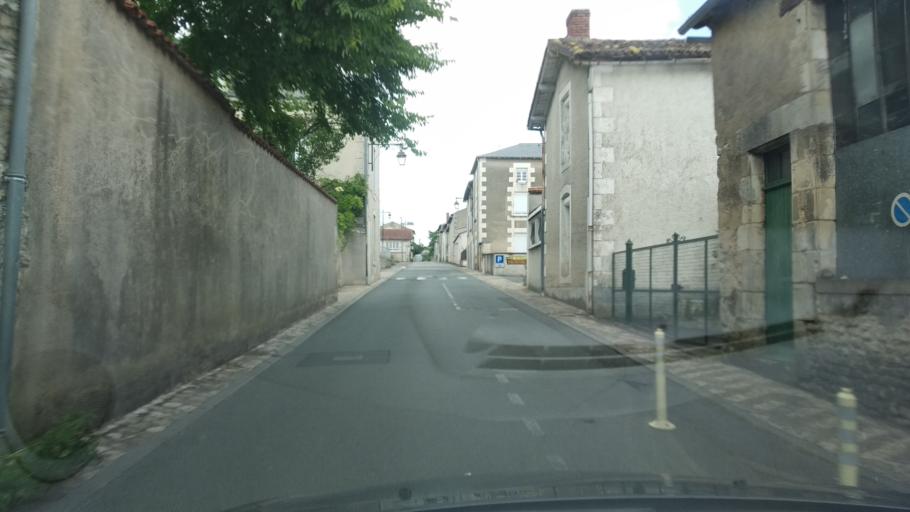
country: FR
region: Poitou-Charentes
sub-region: Departement de la Vienne
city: Vouille
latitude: 46.6406
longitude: 0.1663
